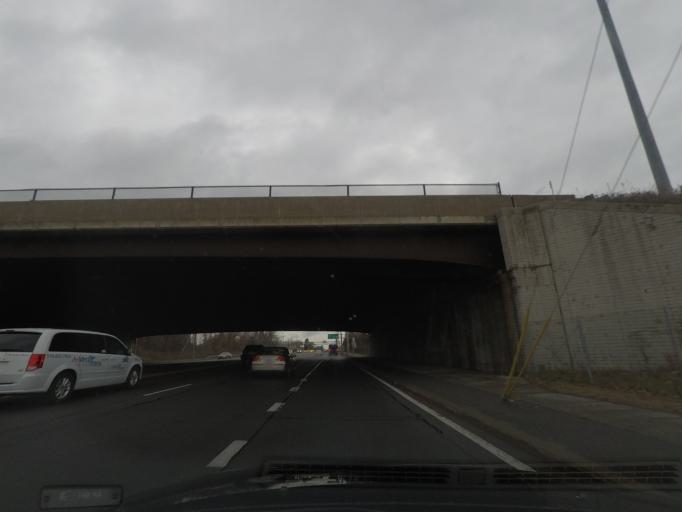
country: US
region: New York
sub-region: Albany County
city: Colonie
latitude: 42.7105
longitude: -73.8245
